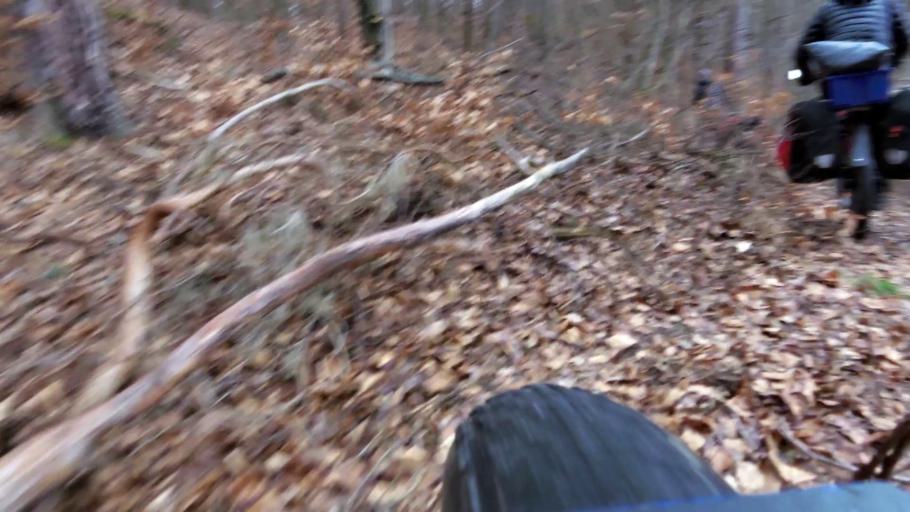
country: PL
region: West Pomeranian Voivodeship
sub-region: Powiat walecki
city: Miroslawiec
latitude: 53.3510
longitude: 16.2622
